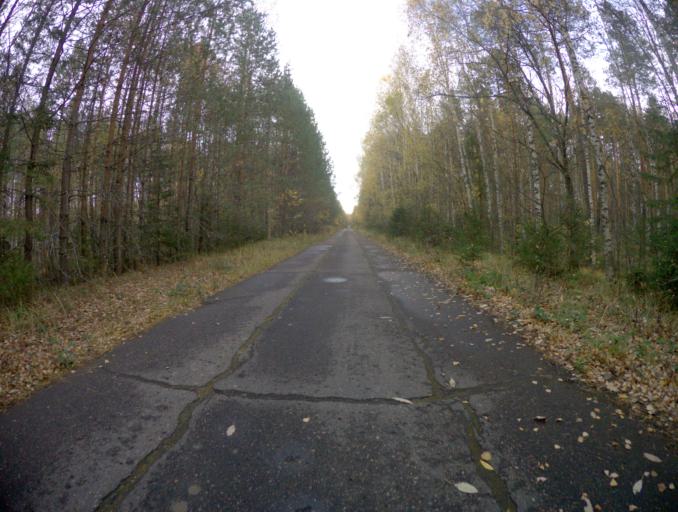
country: RU
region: Vladimir
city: Raduzhnyy
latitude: 55.9323
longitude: 40.3389
